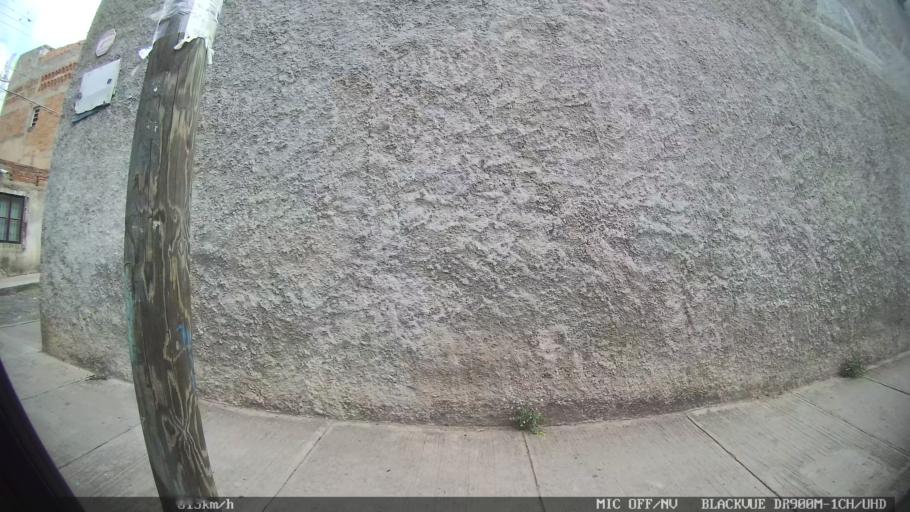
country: MX
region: Jalisco
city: Tonala
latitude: 20.6317
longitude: -103.2381
